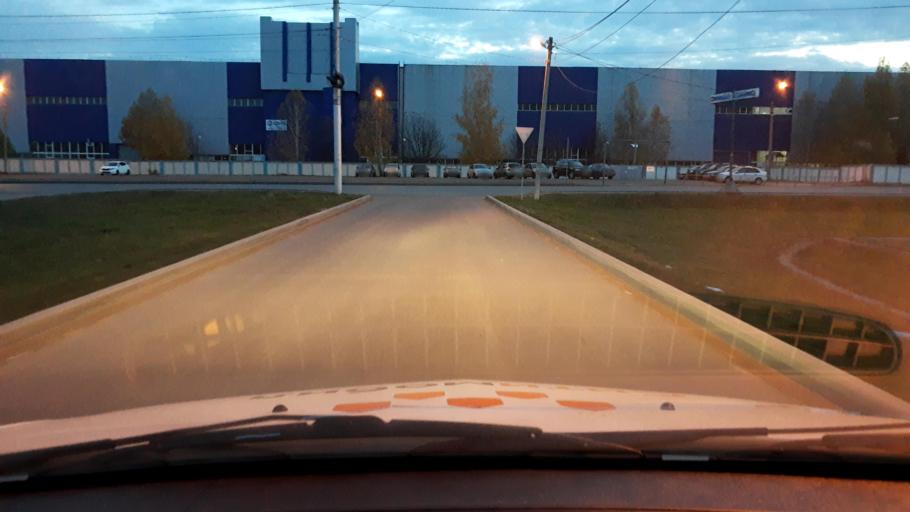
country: RU
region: Bashkortostan
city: Iglino
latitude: 54.7595
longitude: 56.2437
